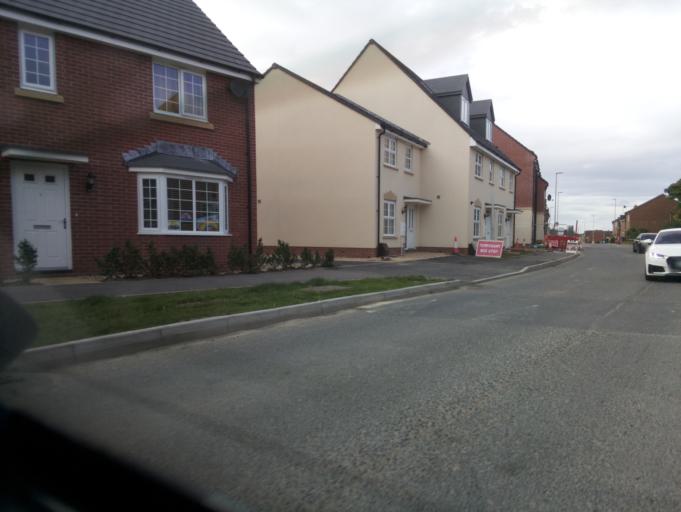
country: GB
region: England
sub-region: Gloucestershire
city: Gloucester
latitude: 51.8186
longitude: -2.2677
